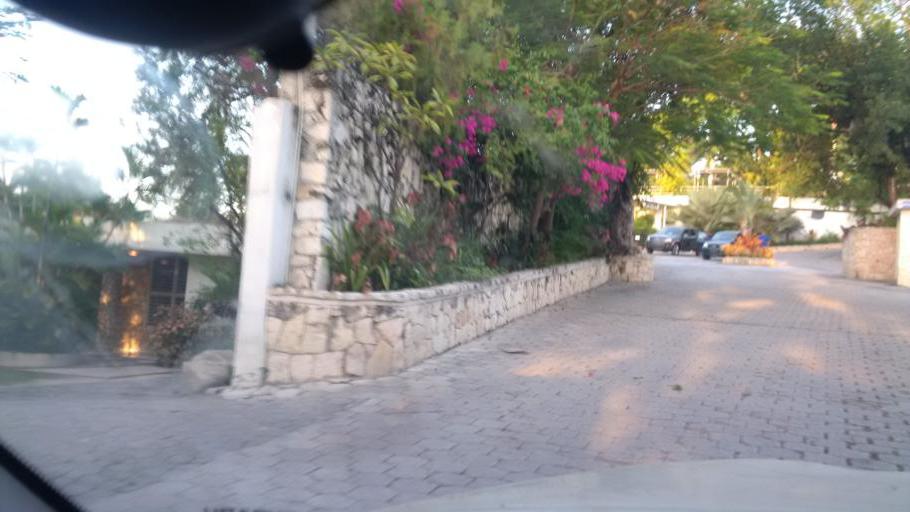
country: HT
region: Ouest
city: Delmas 73
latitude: 18.5275
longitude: -72.2982
